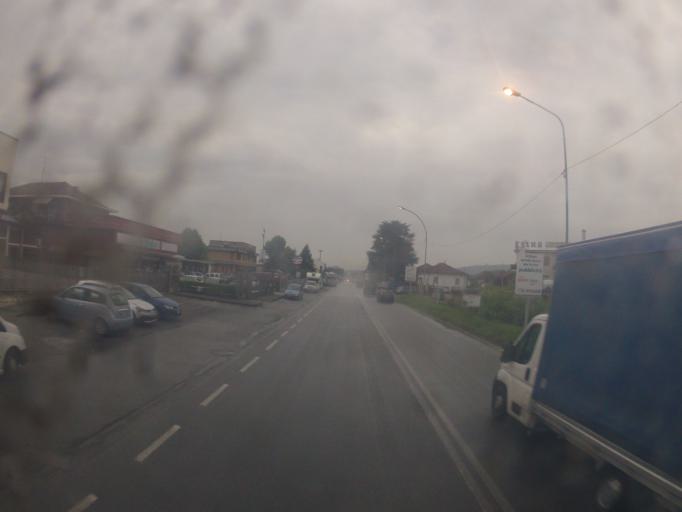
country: IT
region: Piedmont
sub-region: Provincia di Torino
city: Tagliaferro
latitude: 44.9890
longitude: 7.6712
